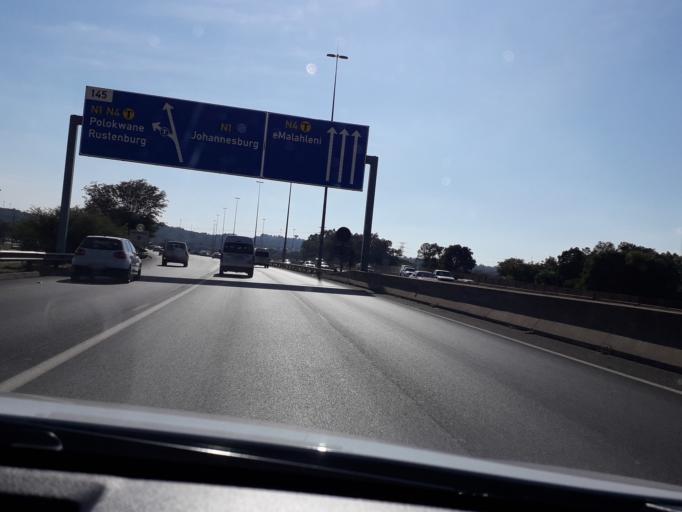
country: ZA
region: Gauteng
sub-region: City of Tshwane Metropolitan Municipality
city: Pretoria
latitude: -25.7415
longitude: 28.2563
